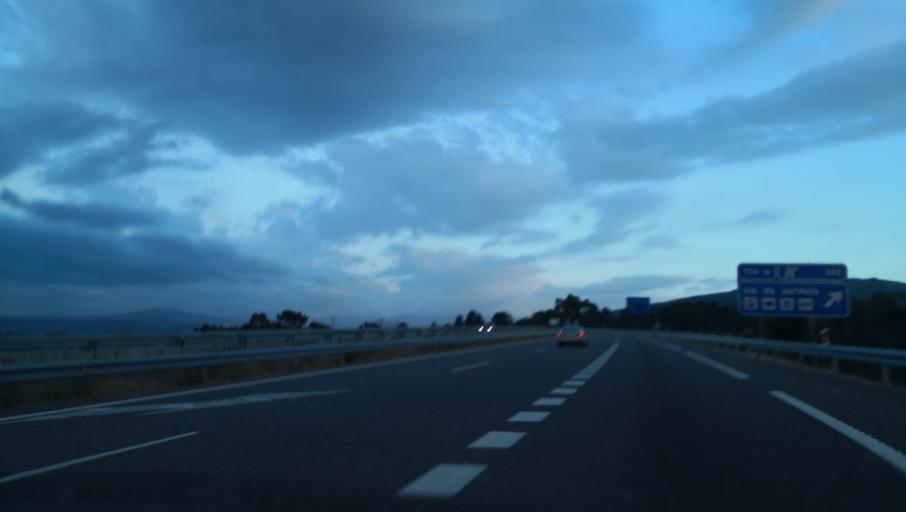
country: ES
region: Galicia
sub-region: Provincia de Ourense
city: Melon
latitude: 42.2766
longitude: -8.2035
